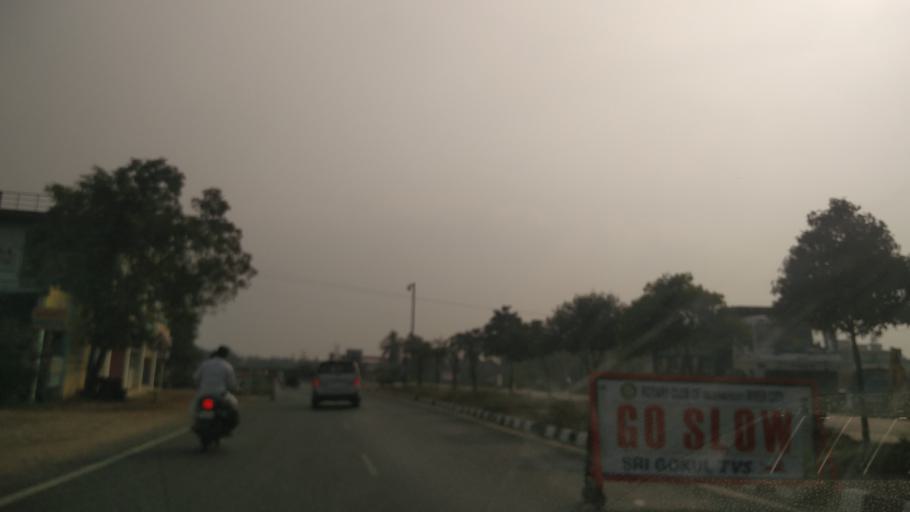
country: IN
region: Andhra Pradesh
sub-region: East Godavari
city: Rajahmundry
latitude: 16.9863
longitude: 81.7988
